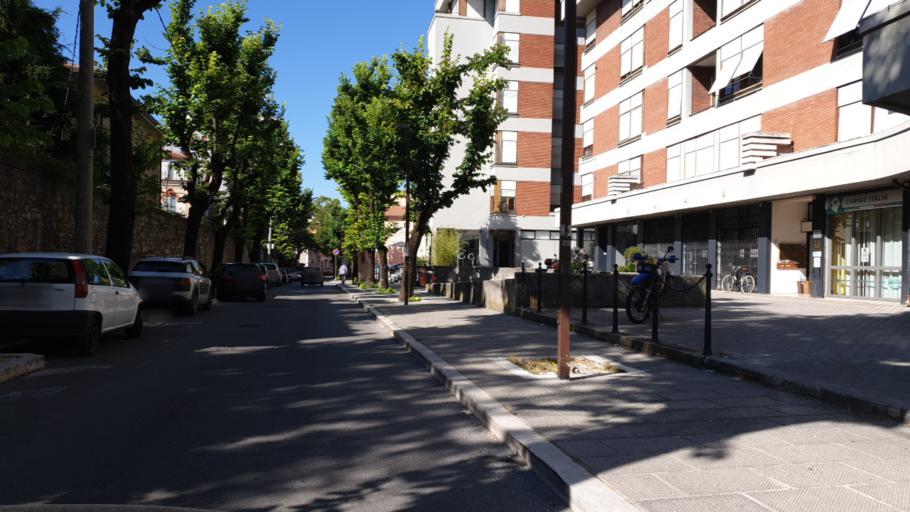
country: IT
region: Umbria
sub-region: Provincia di Perugia
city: Foligno
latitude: 42.9547
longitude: 12.7078
